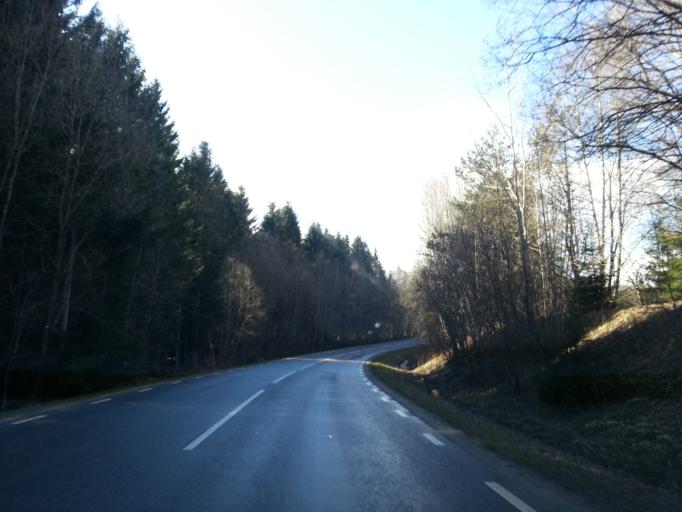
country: SE
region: Vaestra Goetaland
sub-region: Kungalvs Kommun
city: Diserod
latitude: 57.9435
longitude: 12.0103
